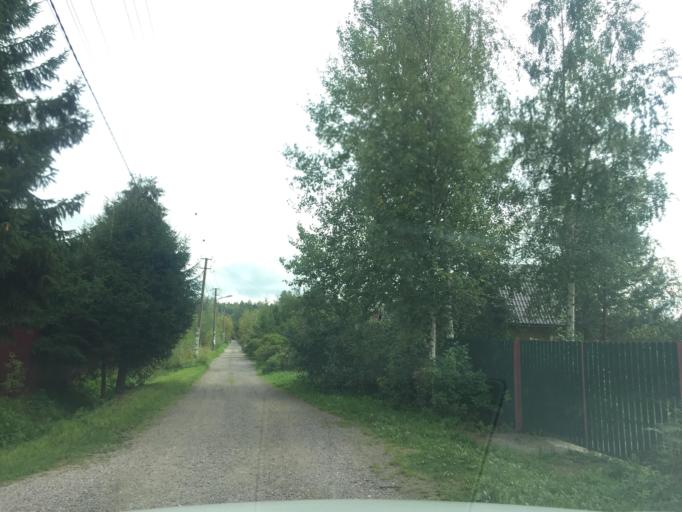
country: RU
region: Leningrad
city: Siverskiy
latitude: 59.2965
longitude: 30.0272
